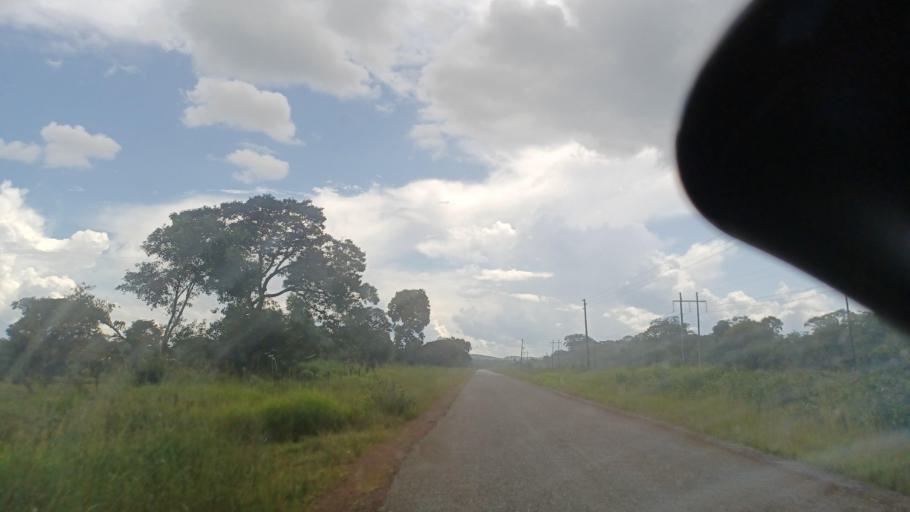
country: ZM
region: North-Western
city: Kasempa
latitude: -13.1030
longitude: 25.8872
